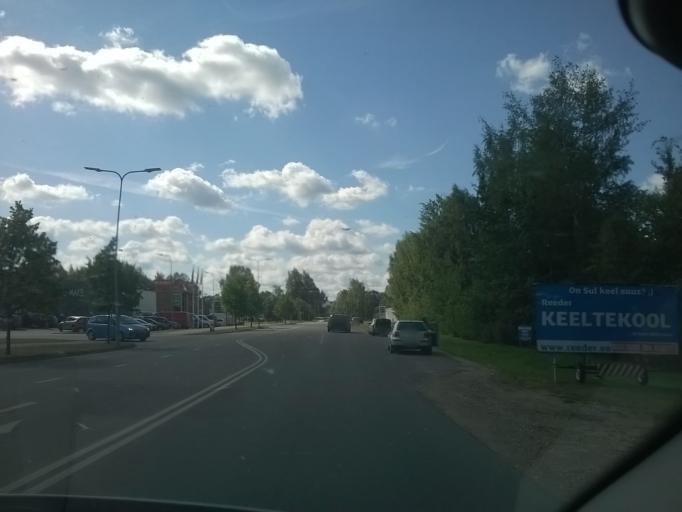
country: EE
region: Vorumaa
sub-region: Voru linn
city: Voru
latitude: 57.8359
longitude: 27.0090
